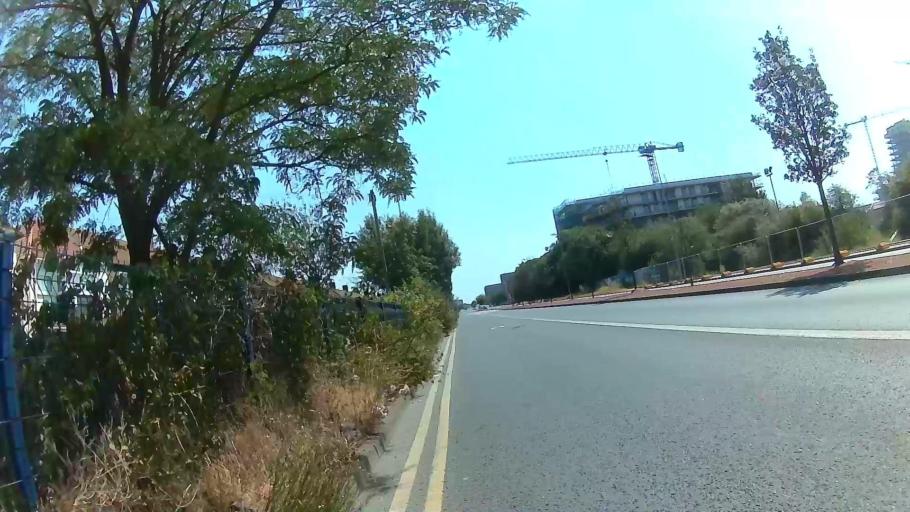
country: GB
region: England
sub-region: Greater London
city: Dagenham
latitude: 51.5274
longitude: 0.1602
